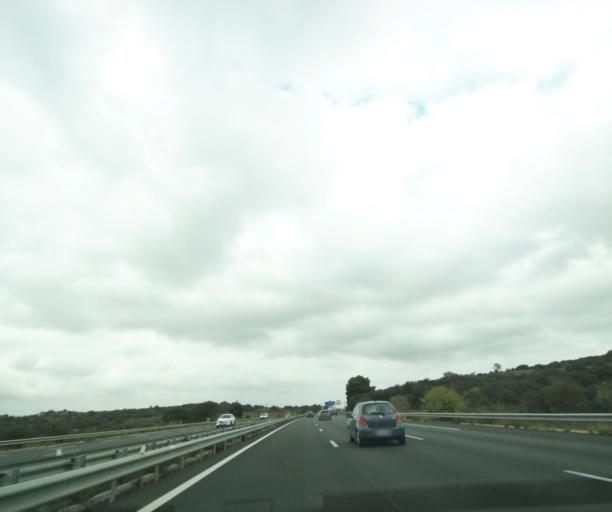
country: FR
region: Languedoc-Roussillon
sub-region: Departement de l'Herault
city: Bessan
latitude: 43.3757
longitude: 3.4082
